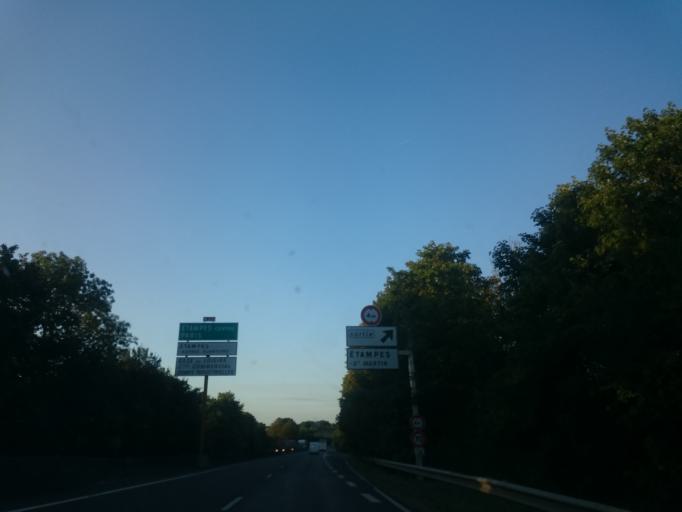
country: FR
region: Ile-de-France
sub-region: Departement de l'Essonne
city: Etampes
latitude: 48.4158
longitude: 2.1303
